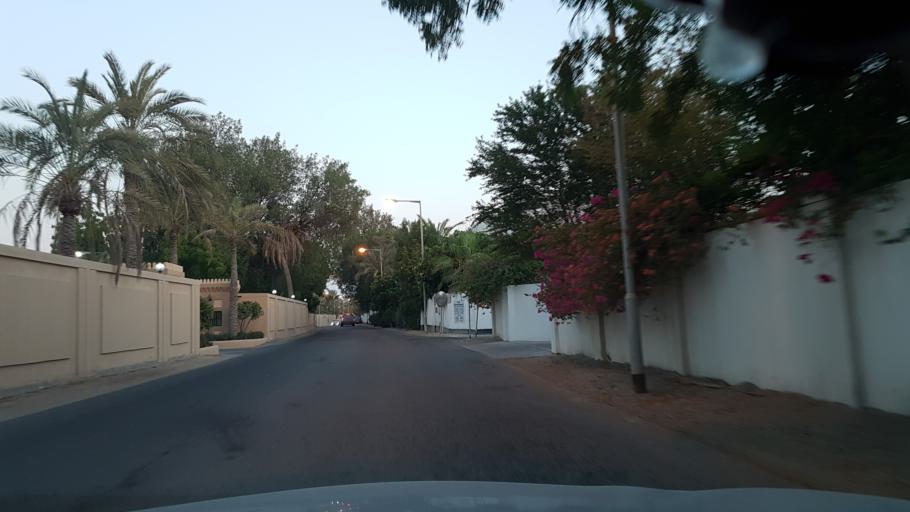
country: BH
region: Manama
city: Jidd Hafs
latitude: 26.2261
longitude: 50.4891
